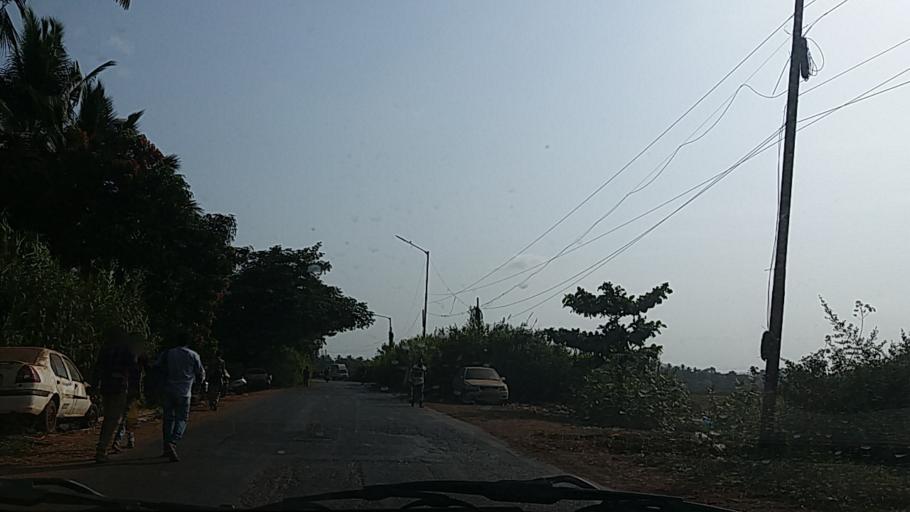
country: IN
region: Goa
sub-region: South Goa
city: Madgaon
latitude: 15.2618
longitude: 73.9696
